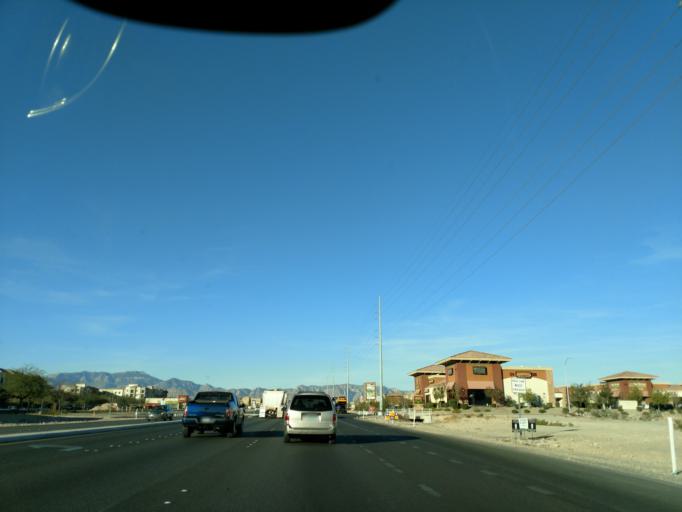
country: US
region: Nevada
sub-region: Clark County
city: Enterprise
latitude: 36.0202
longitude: -115.2647
